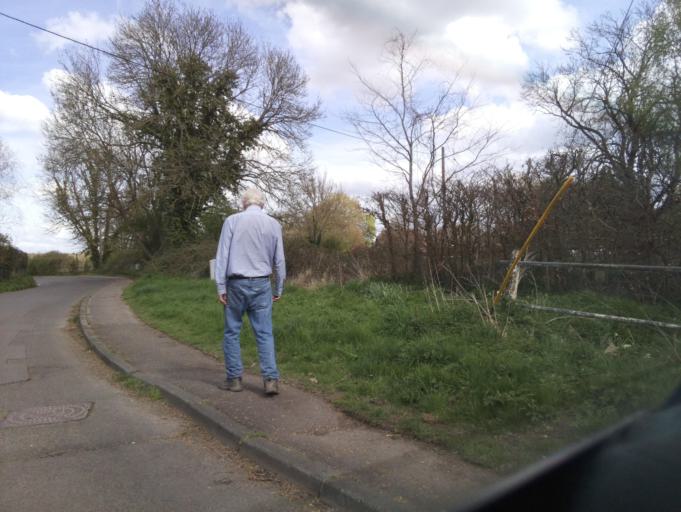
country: GB
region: England
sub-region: Hampshire
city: Romsey
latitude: 51.0859
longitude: -1.5137
